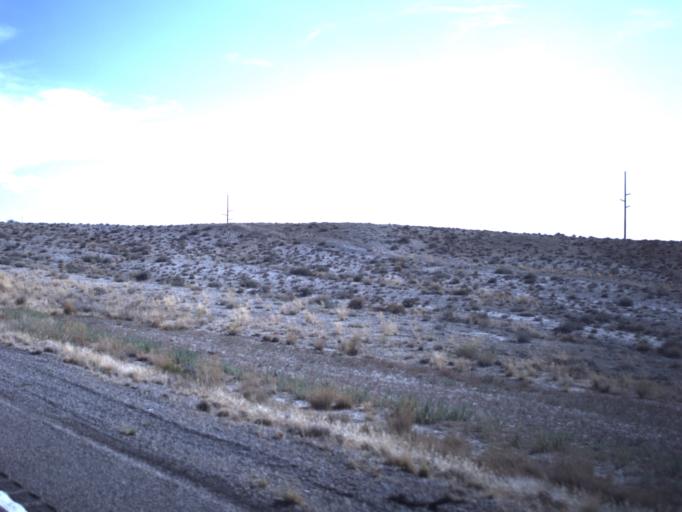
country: US
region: Utah
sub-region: Grand County
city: Moab
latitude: 38.8558
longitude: -109.8040
